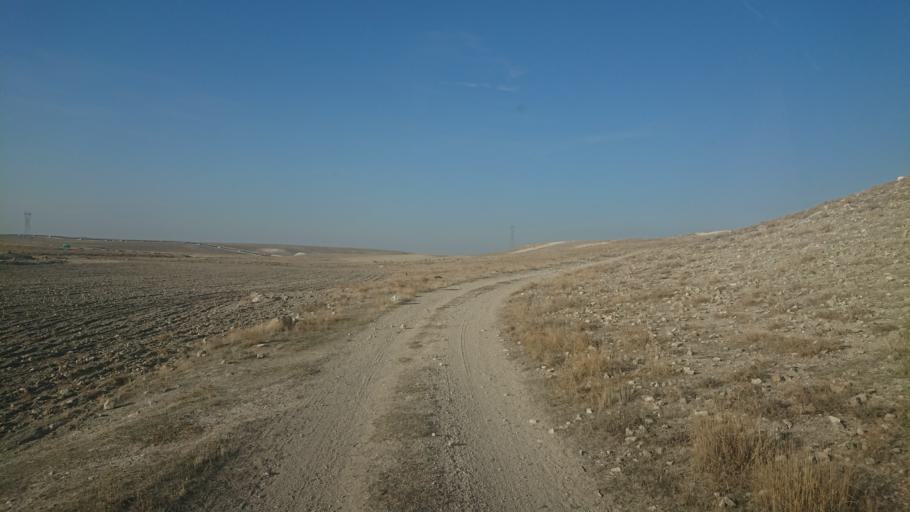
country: TR
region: Aksaray
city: Sultanhani
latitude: 38.1439
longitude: 33.5847
